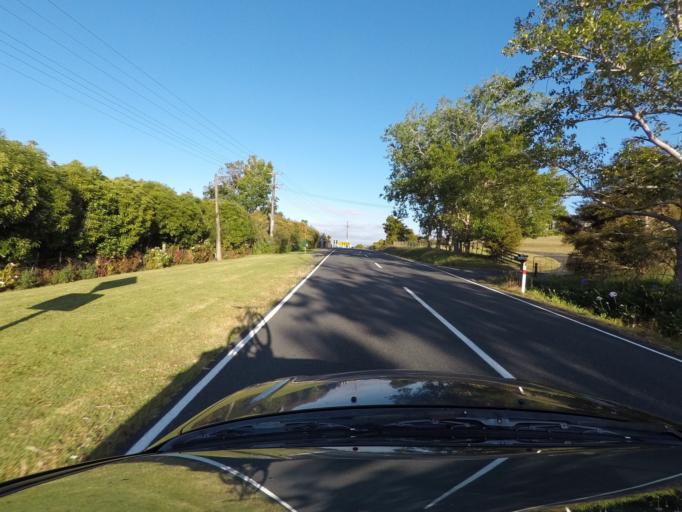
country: NZ
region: Northland
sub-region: Whangarei
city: Whangarei
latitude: -35.6587
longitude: 174.3139
